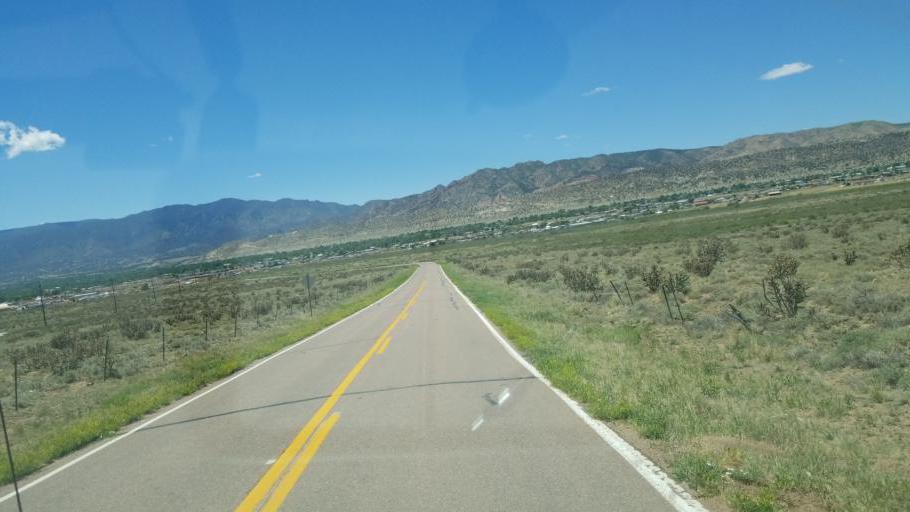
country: US
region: Colorado
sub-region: Fremont County
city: Canon City
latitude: 38.4831
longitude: -105.2184
